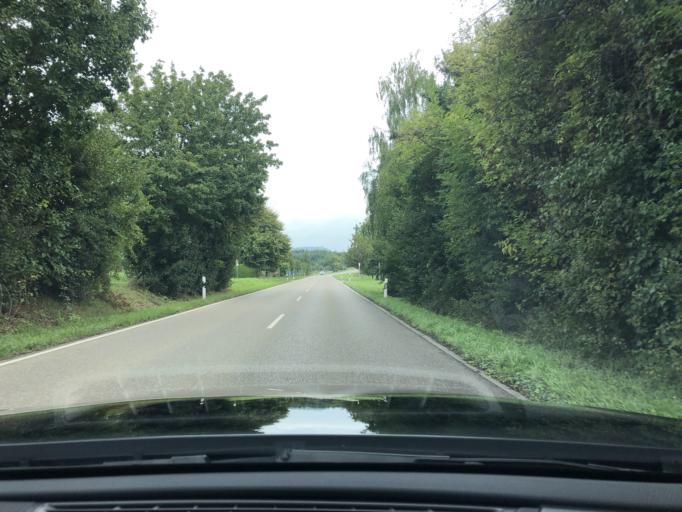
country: DE
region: Baden-Wuerttemberg
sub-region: Regierungsbezirk Stuttgart
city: Marbach am Neckar
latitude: 48.9343
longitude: 9.2738
